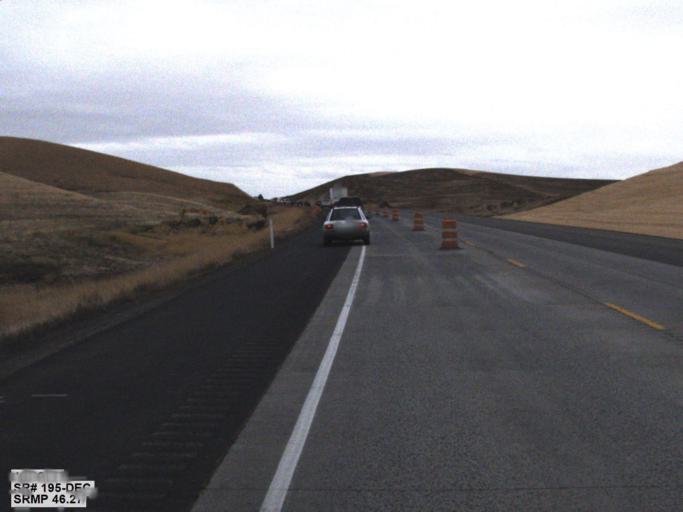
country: US
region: Washington
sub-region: Whitman County
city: Colfax
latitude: 46.9829
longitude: -117.3444
